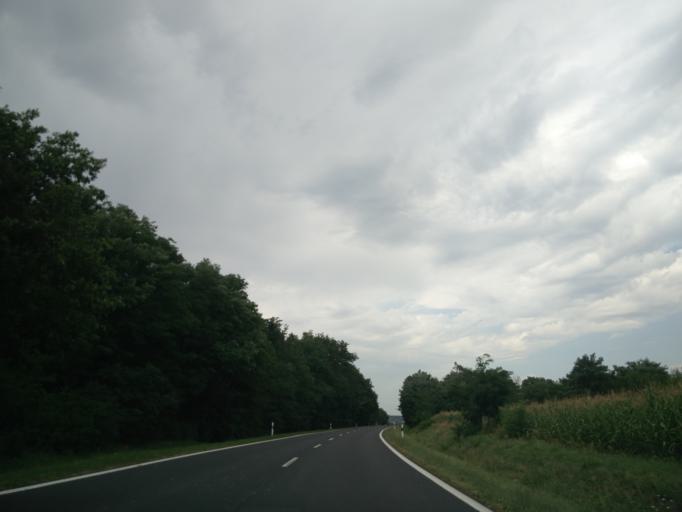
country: HU
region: Vas
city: Janoshaza
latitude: 47.1115
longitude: 17.1576
